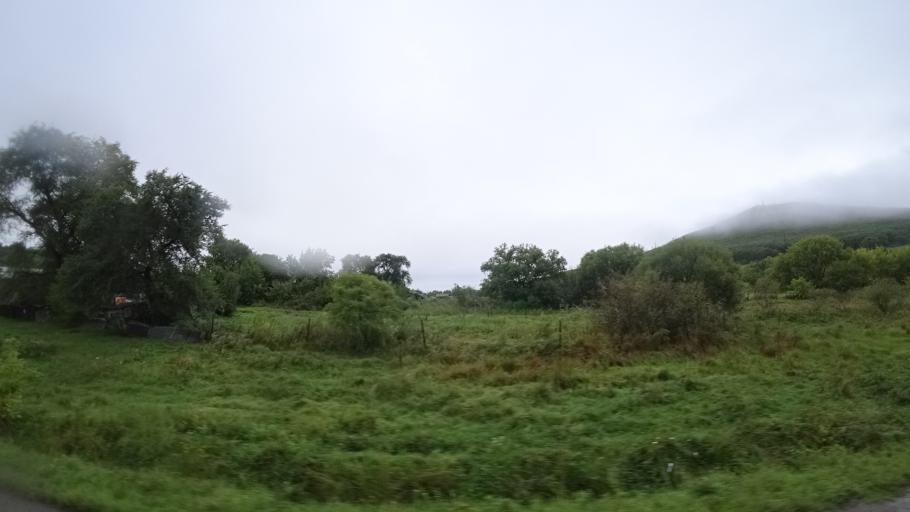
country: RU
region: Primorskiy
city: Monastyrishche
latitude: 44.2577
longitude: 132.4195
